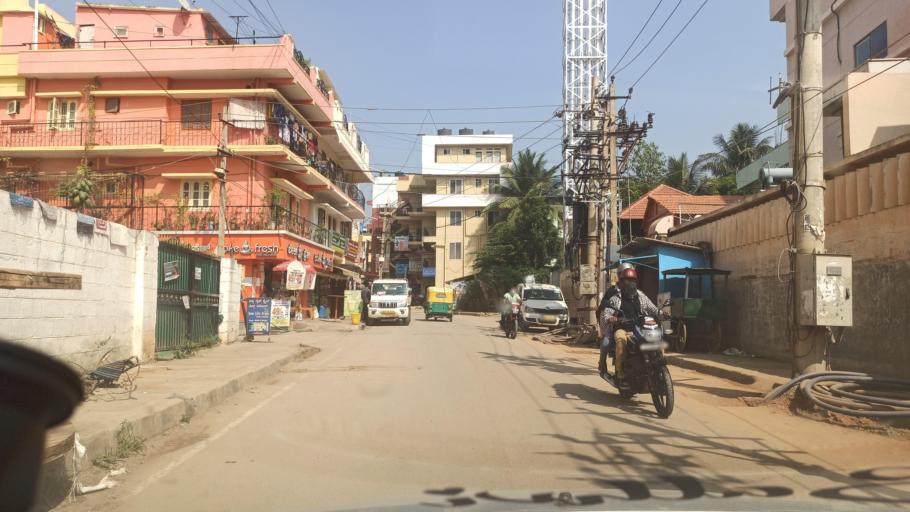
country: IN
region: Karnataka
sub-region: Bangalore Urban
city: Bangalore
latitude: 12.9526
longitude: 77.6981
